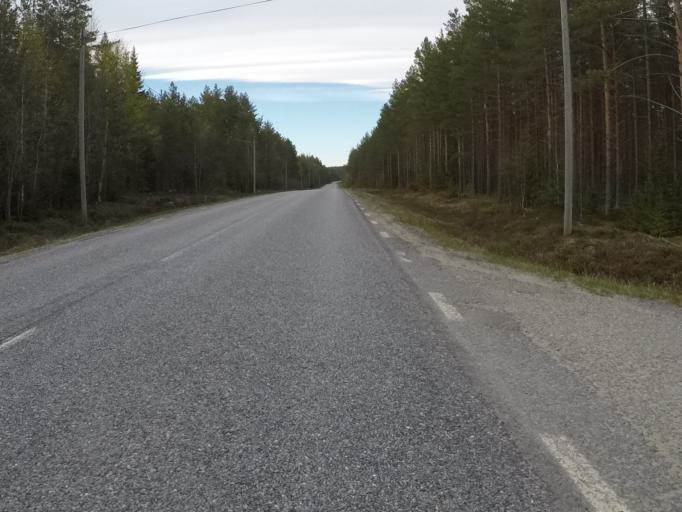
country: SE
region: Vaesterbotten
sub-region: Umea Kommun
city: Saevar
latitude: 63.9460
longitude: 20.7903
